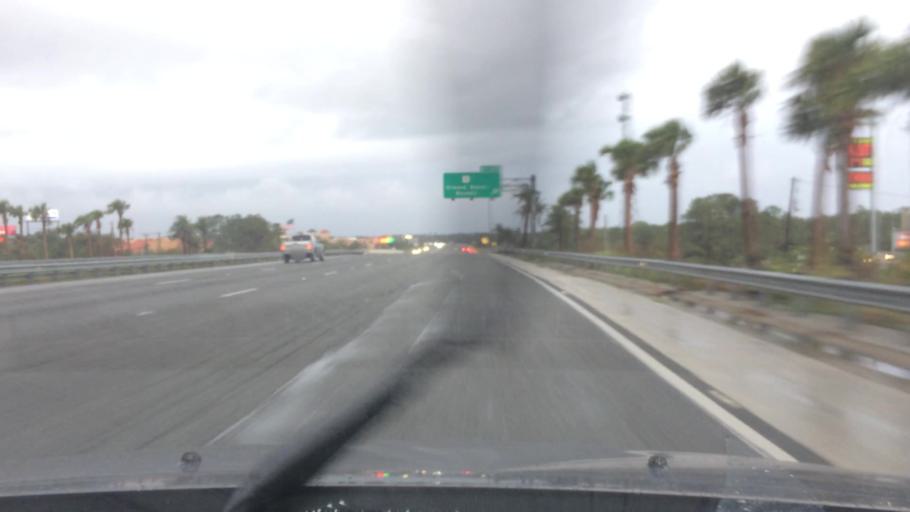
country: US
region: Florida
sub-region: Volusia County
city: Ormond-by-the-Sea
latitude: 29.3343
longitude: -81.1310
